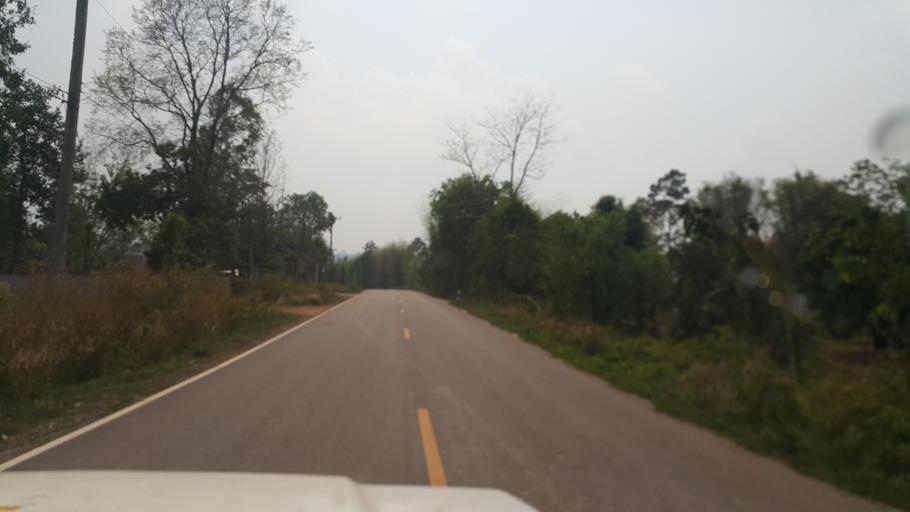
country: TH
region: Nakhon Phanom
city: Ban Phaeng
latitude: 17.9550
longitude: 104.1742
